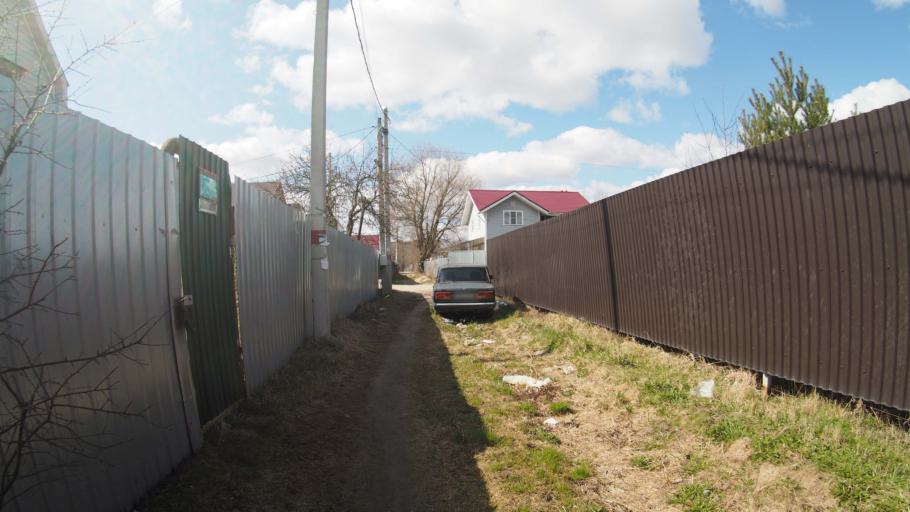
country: RU
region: Moskovskaya
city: Malyshevo
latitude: 55.5471
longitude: 38.3180
